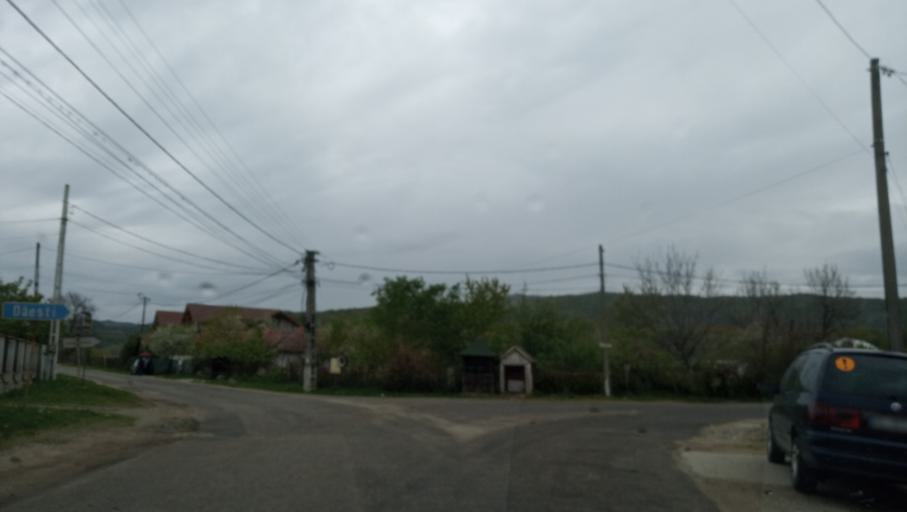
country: RO
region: Valcea
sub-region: Oras Calimanesti
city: Jiblea Veche
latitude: 45.2378
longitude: 24.3645
